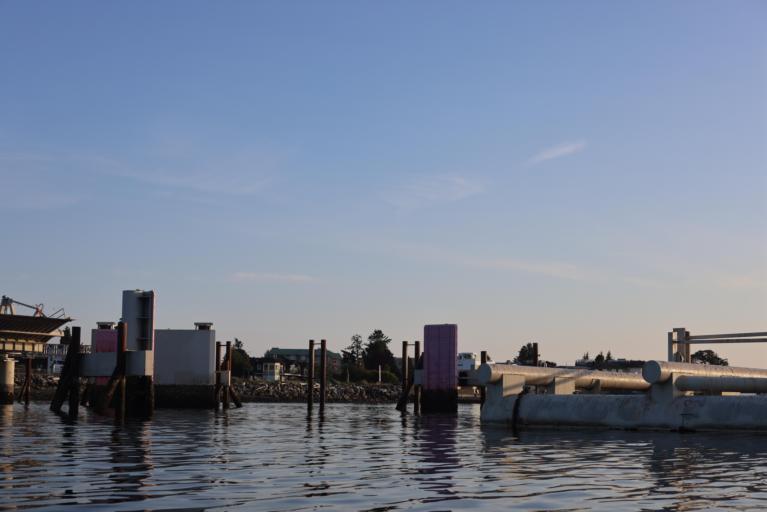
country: CA
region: British Columbia
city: North Saanich
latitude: 48.6423
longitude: -123.3964
